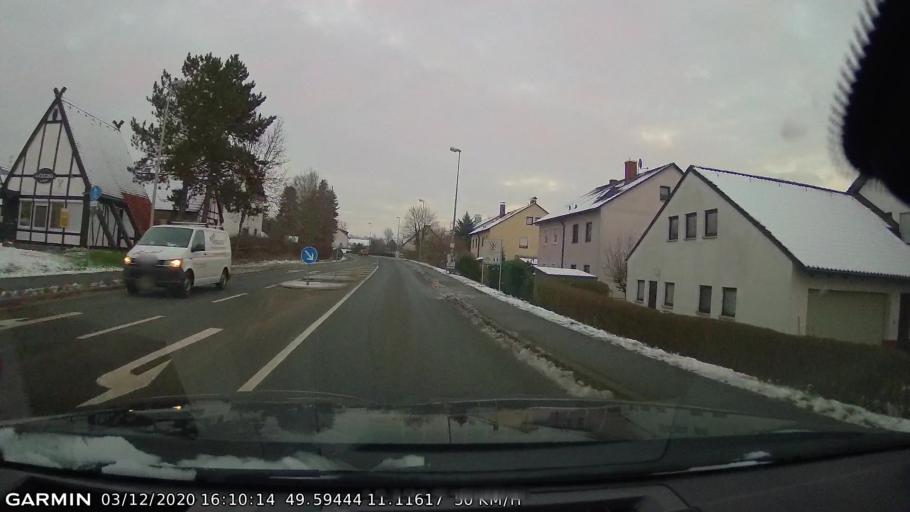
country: DE
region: Bavaria
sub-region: Upper Franconia
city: Dormitz
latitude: 49.5945
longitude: 11.1163
